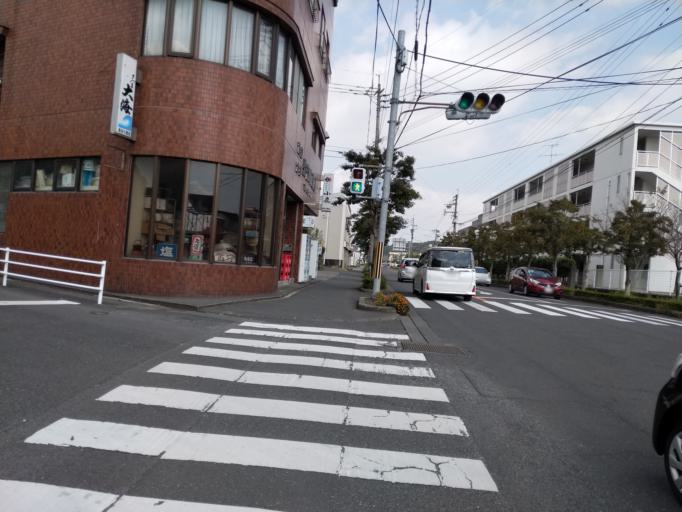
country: JP
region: Kagoshima
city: Kanoya
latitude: 31.3919
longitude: 130.8524
